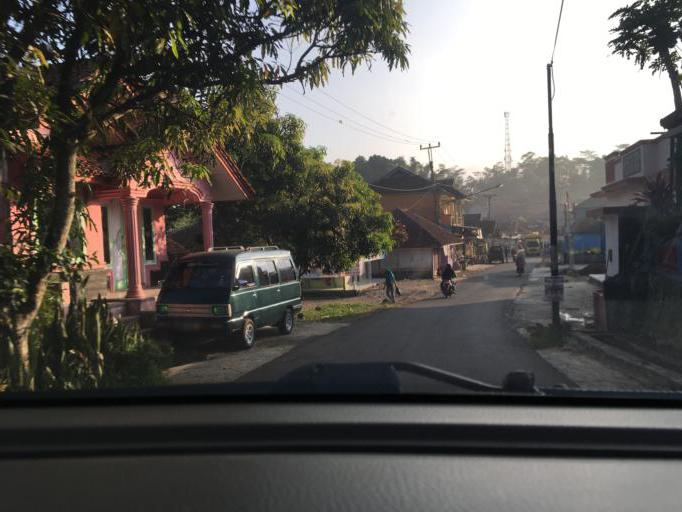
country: ID
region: West Java
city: Maniis
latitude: -7.0398
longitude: 108.3137
